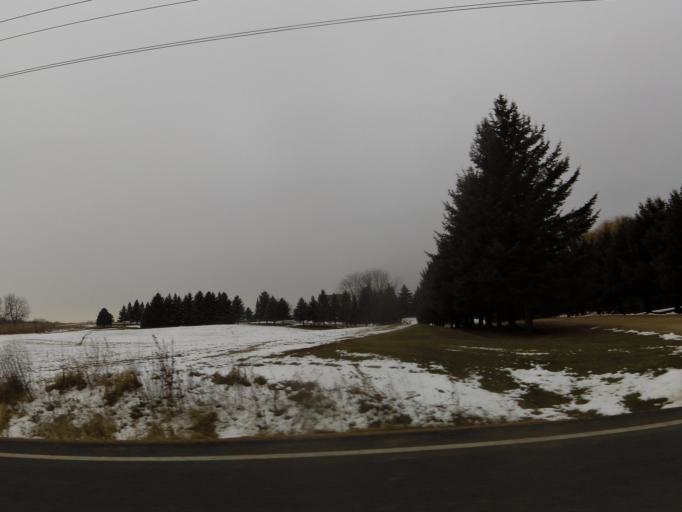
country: US
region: Minnesota
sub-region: Scott County
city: Prior Lake
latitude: 44.6773
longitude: -93.4603
